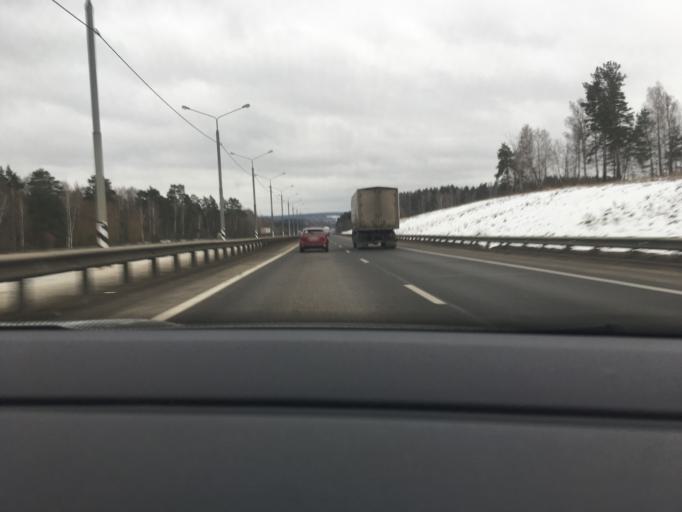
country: RU
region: Tula
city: Zaokskiy
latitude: 54.7904
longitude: 37.4867
